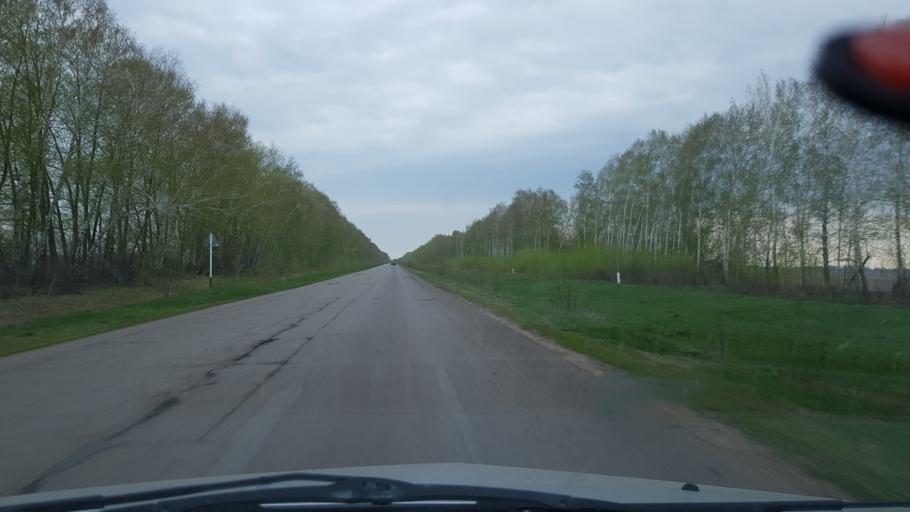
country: RU
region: Samara
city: Podstepki
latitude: 53.6615
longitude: 49.2091
